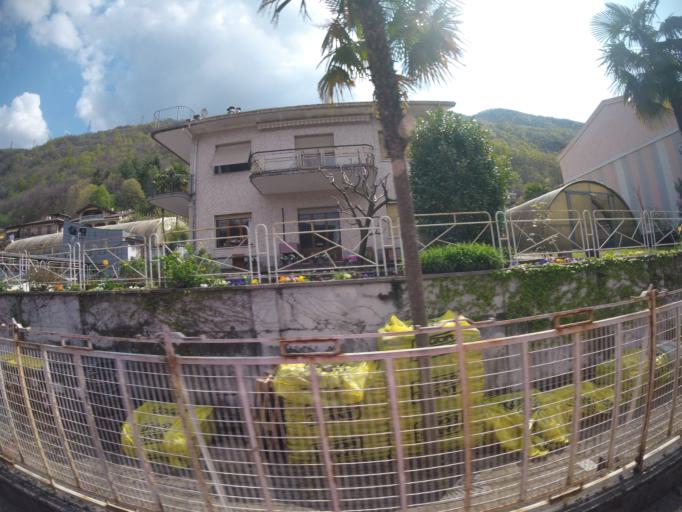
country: IT
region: Piedmont
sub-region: Provincia Verbano-Cusio-Ossola
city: Omegna
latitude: 45.8641
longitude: 8.4130
